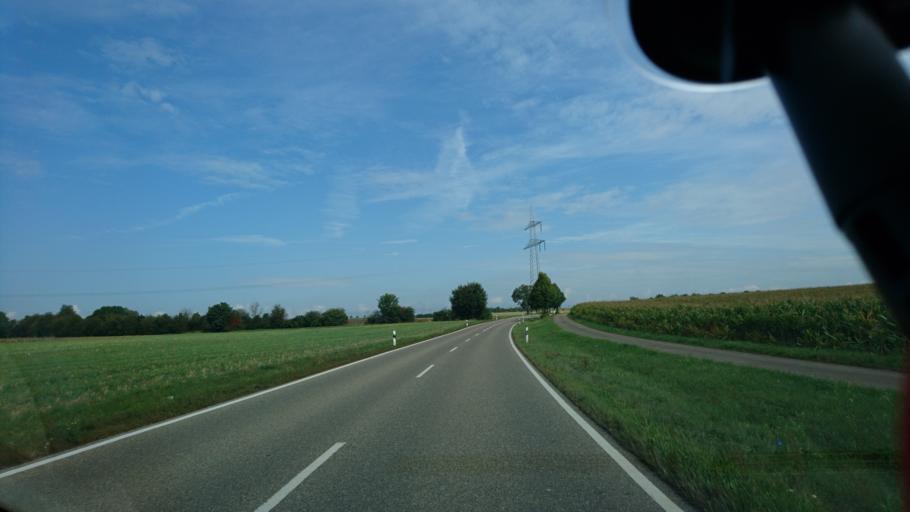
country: DE
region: Baden-Wuerttemberg
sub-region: Regierungsbezirk Stuttgart
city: Vellberg
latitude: 49.1114
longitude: 9.8855
